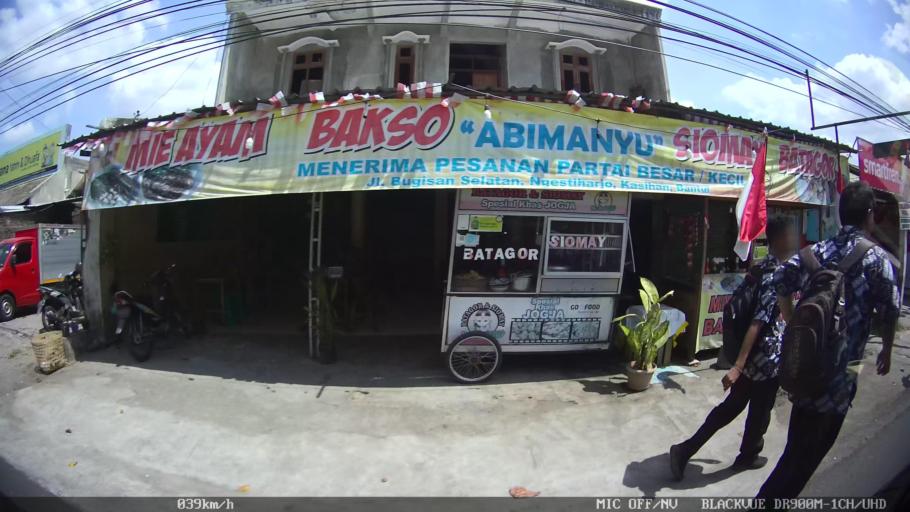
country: ID
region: Daerah Istimewa Yogyakarta
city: Kasihan
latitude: -7.8156
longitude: 110.3487
